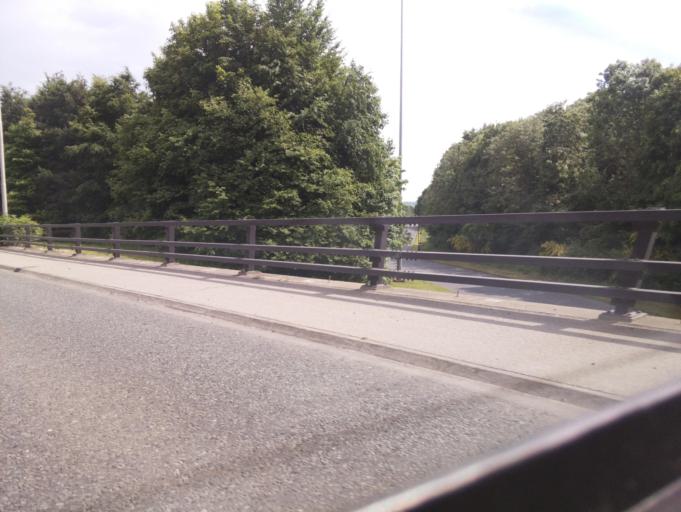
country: GB
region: England
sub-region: Sunderland
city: Washington
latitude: 54.9055
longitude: -1.5146
